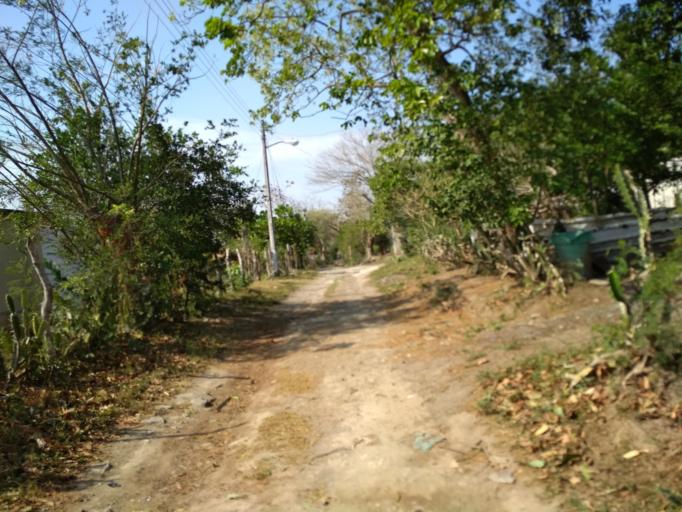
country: MX
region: Veracruz
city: Manlio Fabio Altamirano
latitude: 19.1520
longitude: -96.3087
